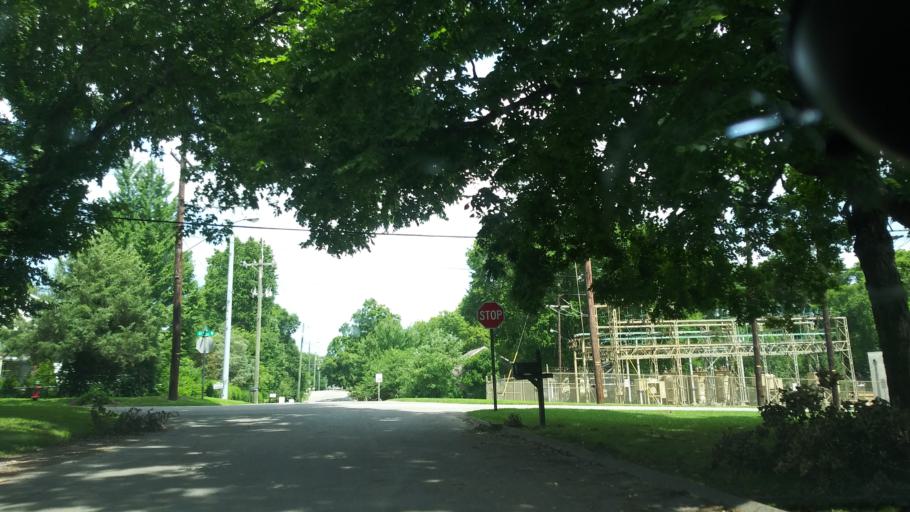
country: US
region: Tennessee
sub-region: Davidson County
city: Belle Meade
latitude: 36.1421
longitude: -86.8359
